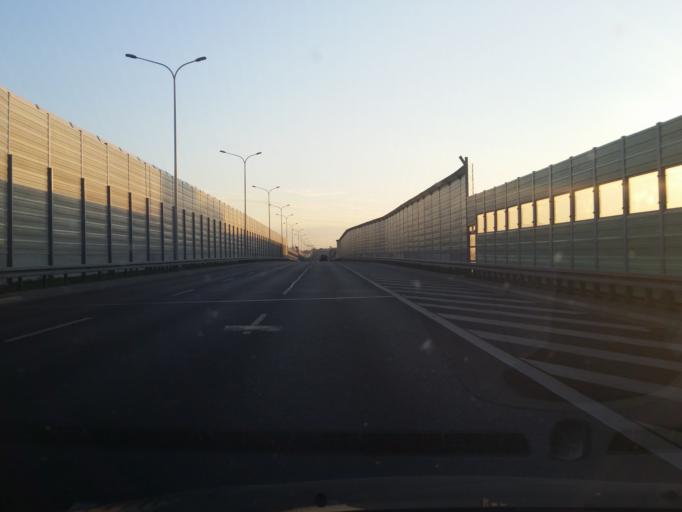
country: PL
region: Masovian Voivodeship
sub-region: Warszawa
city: Bialoleka
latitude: 52.3141
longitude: 20.9688
